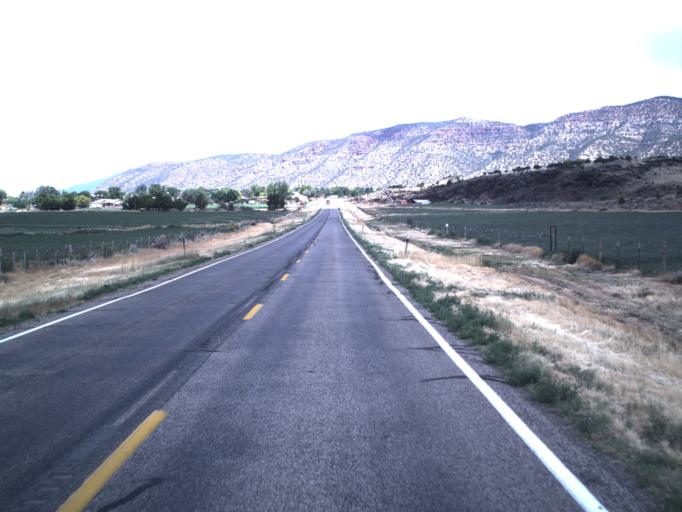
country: US
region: Utah
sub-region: Iron County
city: Parowan
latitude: 37.8769
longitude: -112.7840
